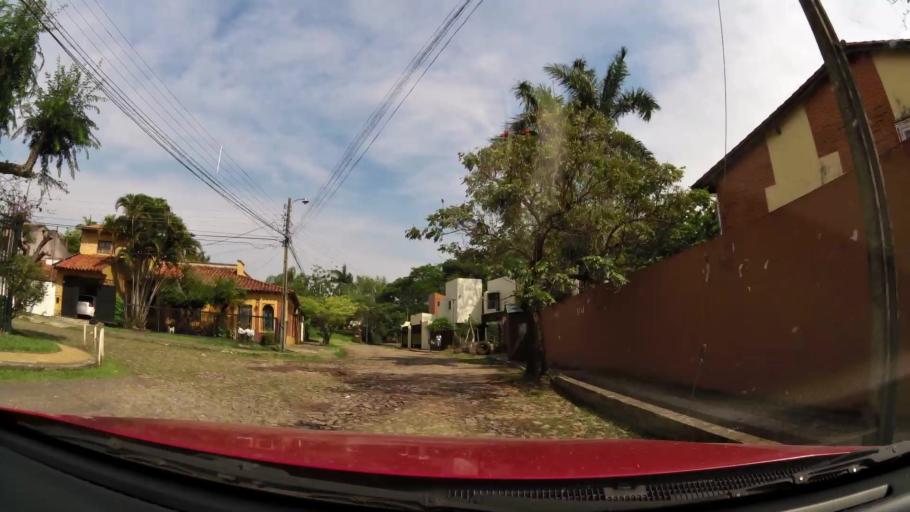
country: PY
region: Asuncion
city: Asuncion
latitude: -25.2648
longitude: -57.5631
